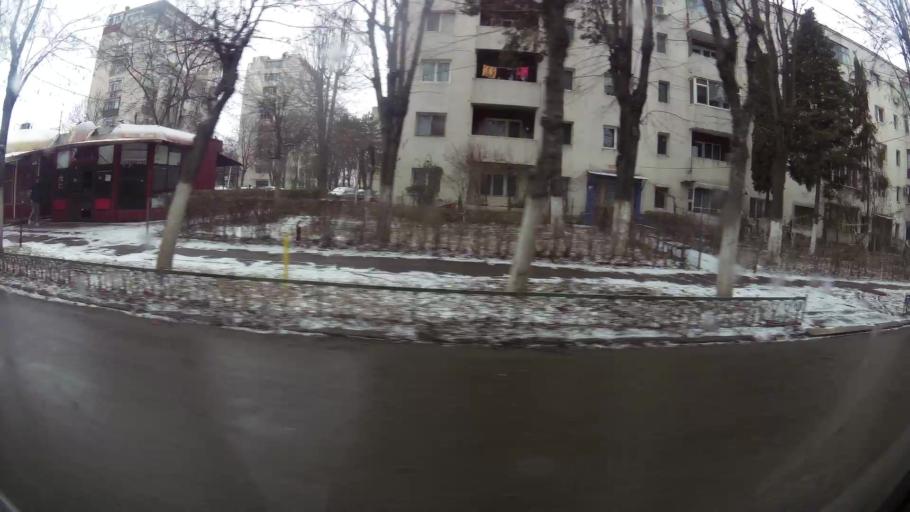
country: RO
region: Prahova
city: Ploiesti
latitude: 44.9597
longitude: 26.0004
